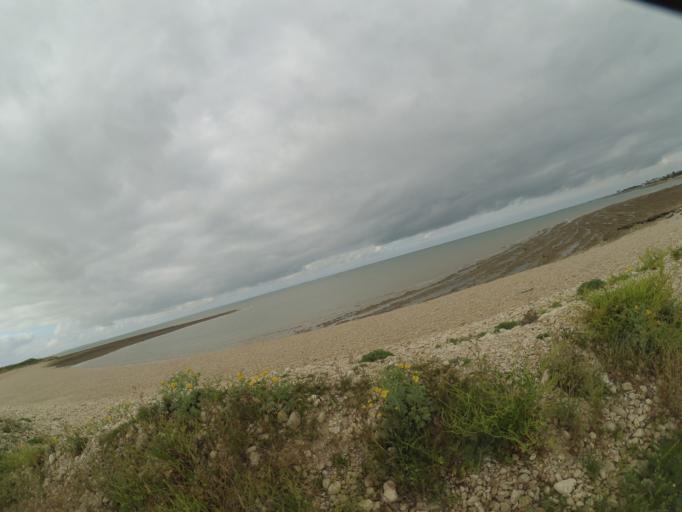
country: FR
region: Poitou-Charentes
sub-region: Departement de la Charente-Maritime
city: La Rochelle
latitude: 46.1330
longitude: -1.1489
